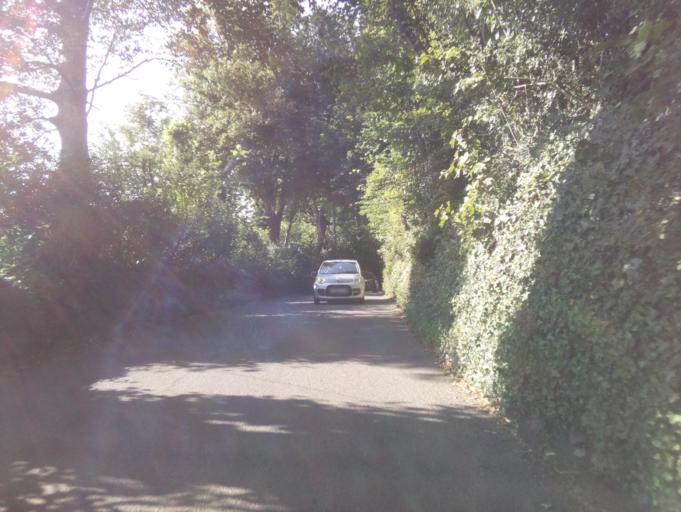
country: GB
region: England
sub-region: Devon
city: Ashburton
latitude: 50.5106
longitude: -3.7663
